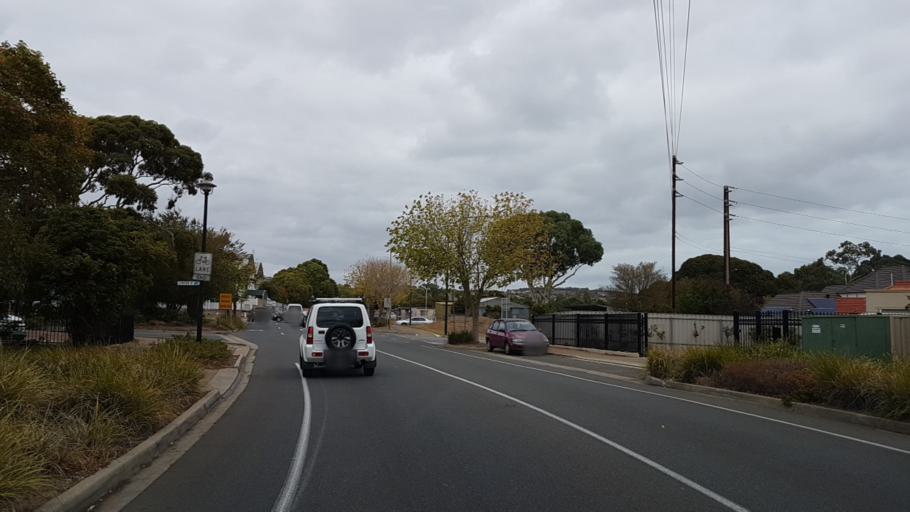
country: AU
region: South Australia
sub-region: Marion
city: Marion
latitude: -35.0160
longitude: 138.5643
